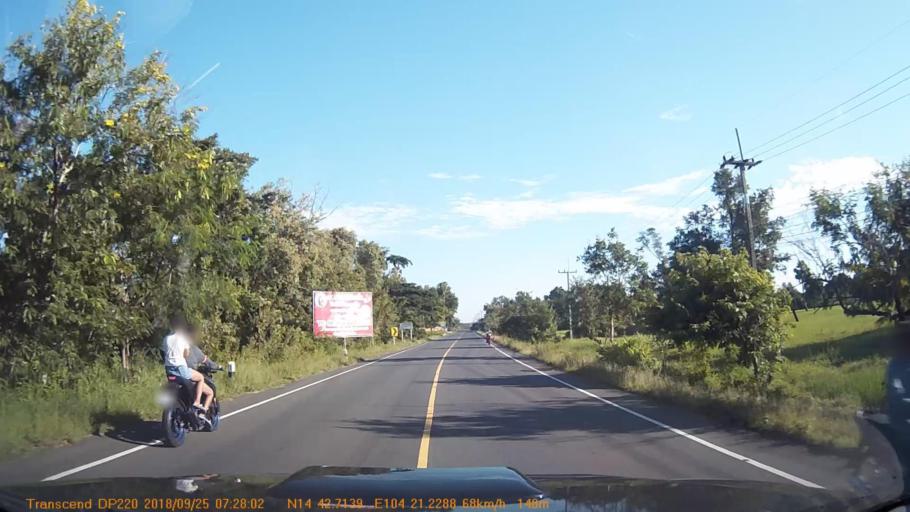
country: TH
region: Sisaket
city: Phrai Bueng
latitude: 14.7123
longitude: 104.3538
